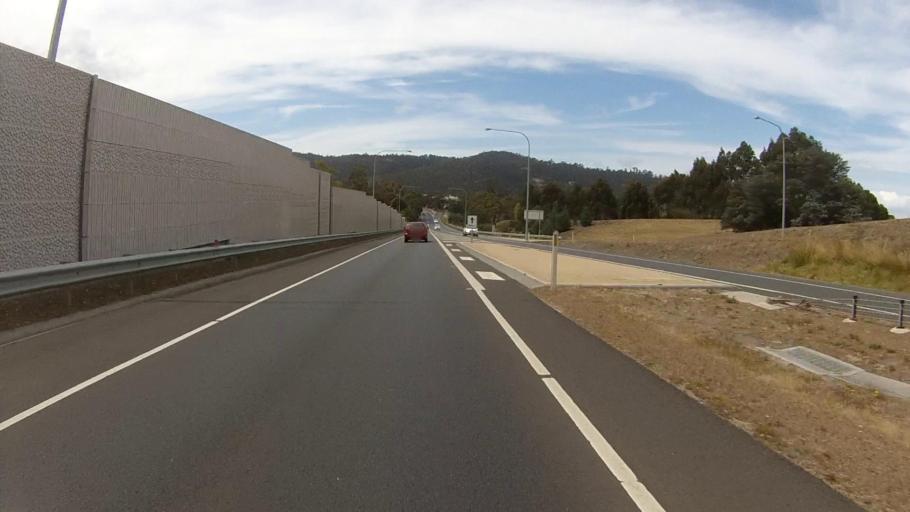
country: AU
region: Tasmania
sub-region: Kingborough
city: Kingston
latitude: -42.9740
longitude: 147.3042
